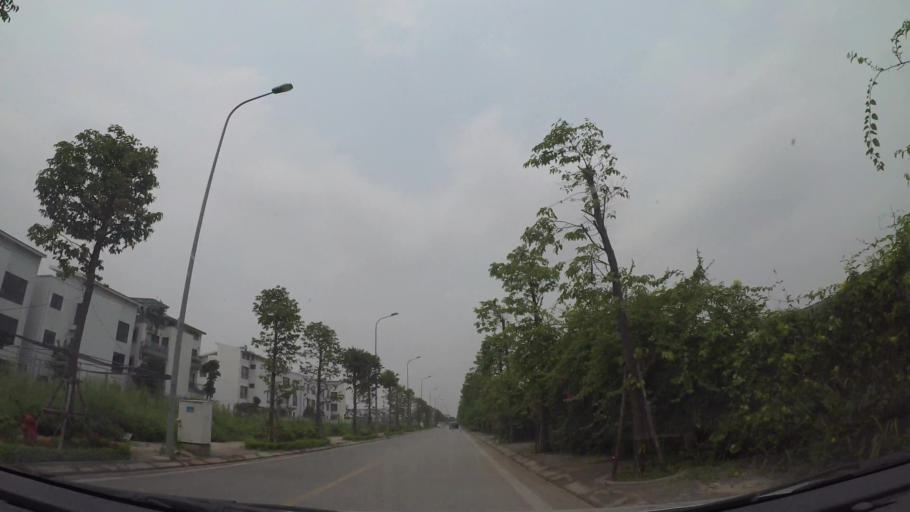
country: VN
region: Ha Noi
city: Cau Dien
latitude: 21.0260
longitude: 105.7467
